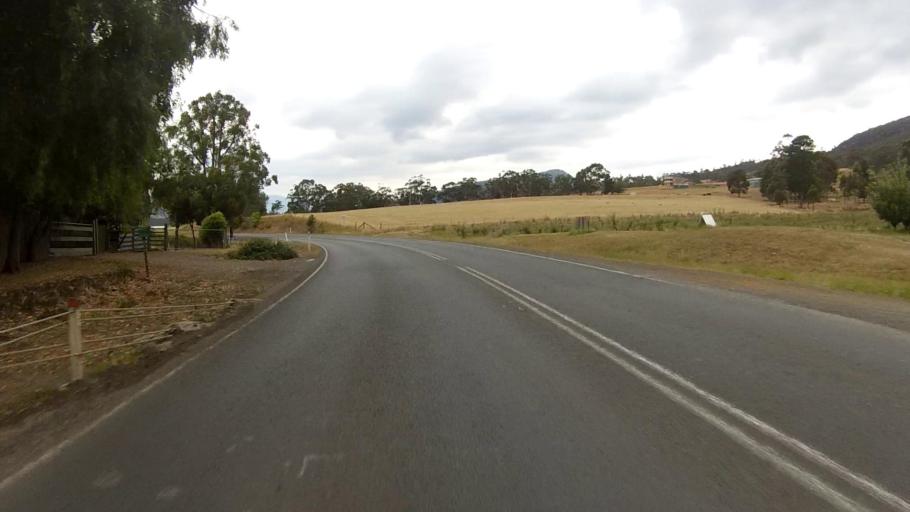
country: AU
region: Tasmania
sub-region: Huon Valley
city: Franklin
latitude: -43.0883
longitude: 147.0292
